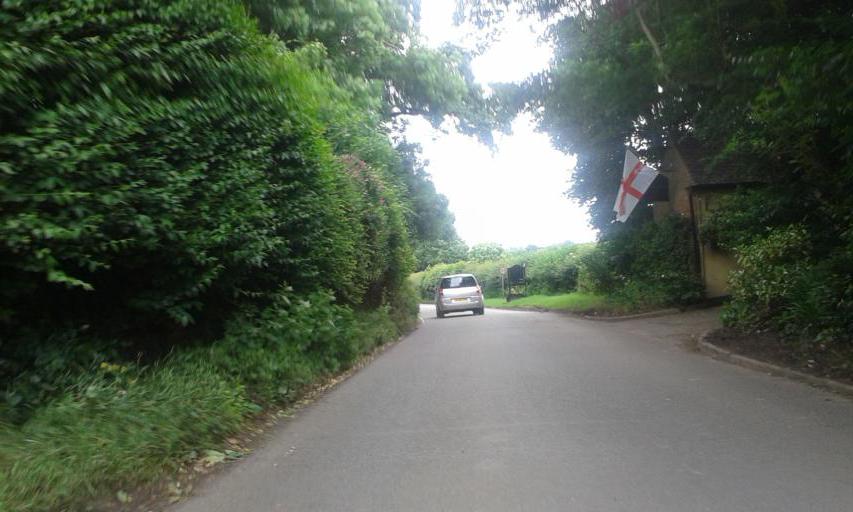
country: GB
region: England
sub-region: Leicestershire
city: Croft
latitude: 52.5884
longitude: -1.2586
